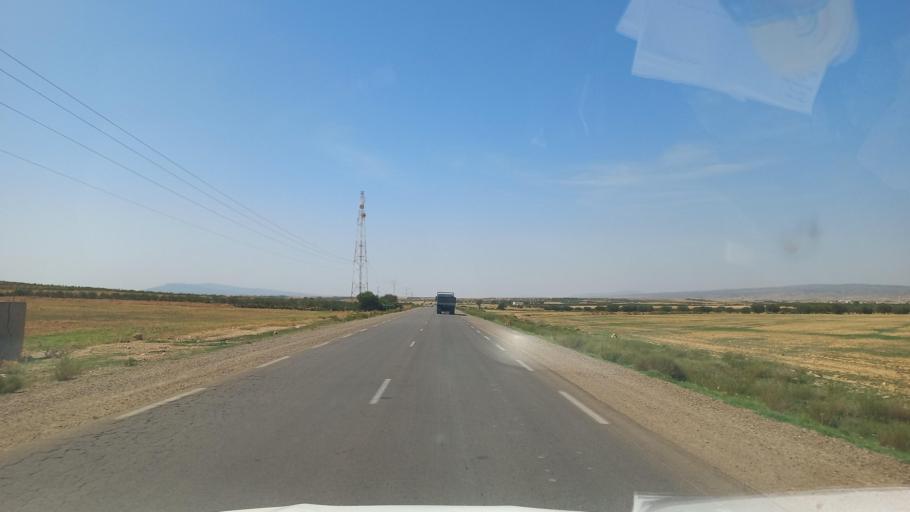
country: TN
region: Al Qasrayn
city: Sbiba
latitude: 35.3768
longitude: 9.1051
